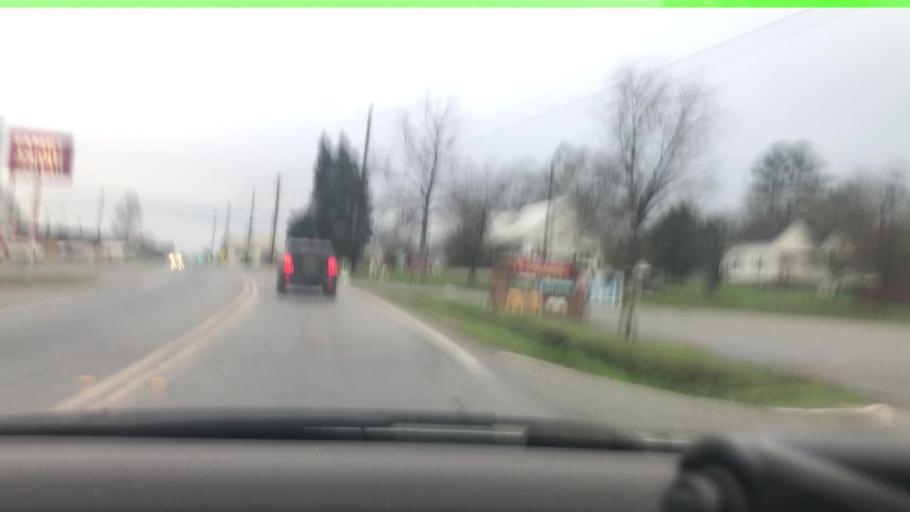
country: US
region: Georgia
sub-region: Oglethorpe County
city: Lexington
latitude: 33.8817
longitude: -83.1582
